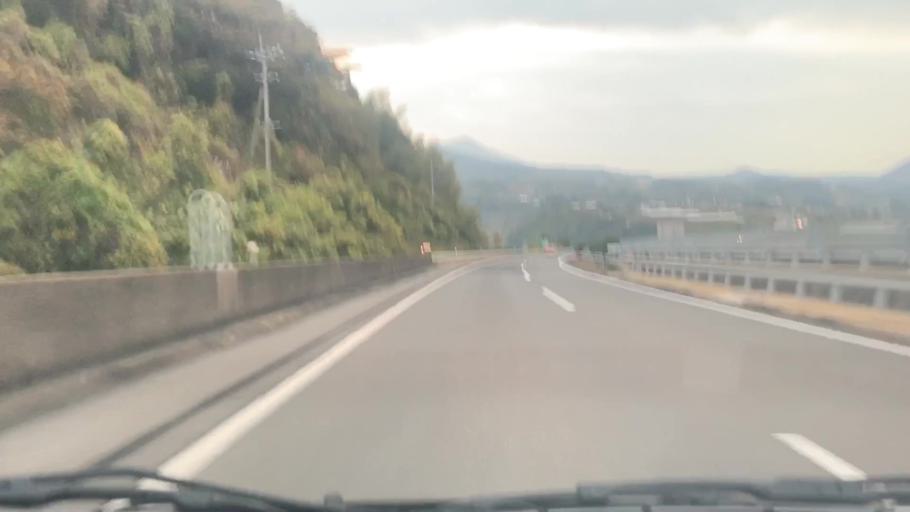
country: JP
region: Nagasaki
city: Omura
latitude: 33.0264
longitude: 129.9381
